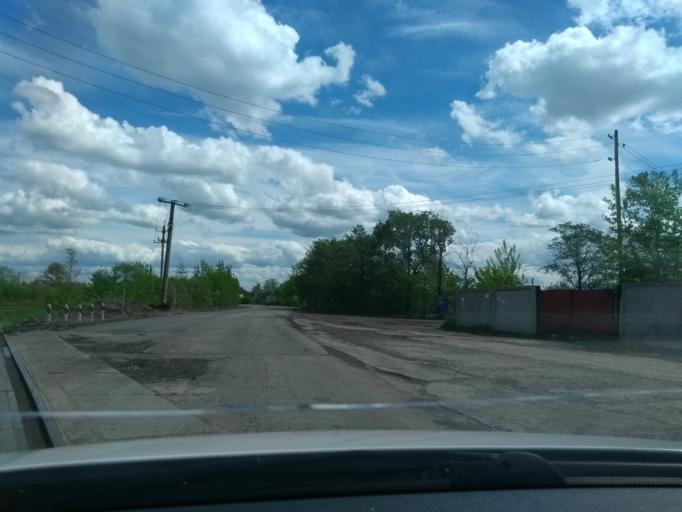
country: RU
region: Perm
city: Kondratovo
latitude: 58.0105
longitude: 56.0751
